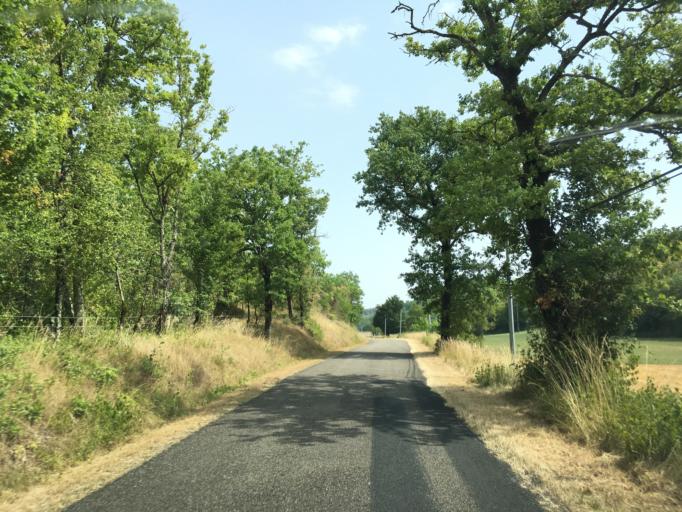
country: FR
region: Midi-Pyrenees
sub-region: Departement du Lot
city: Le Vigan
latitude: 44.7466
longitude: 1.5244
